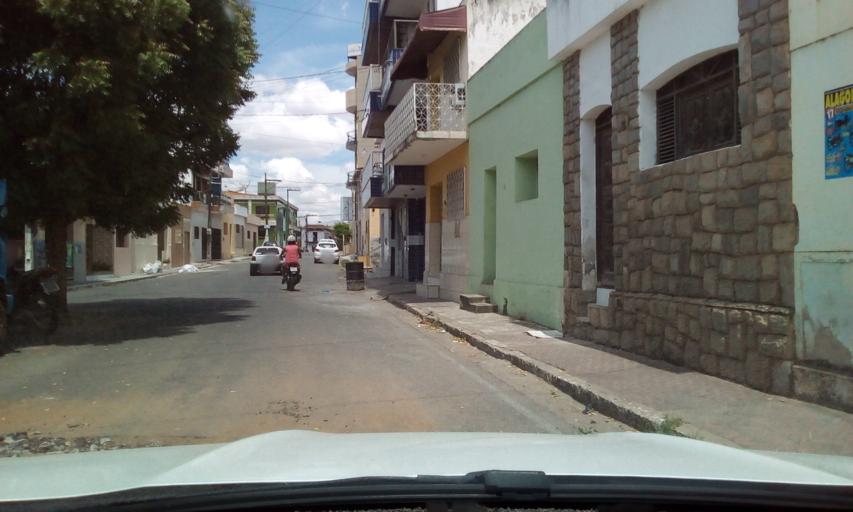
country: BR
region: Paraiba
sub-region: Guarabira
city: Guarabira
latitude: -6.8528
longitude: -35.4876
